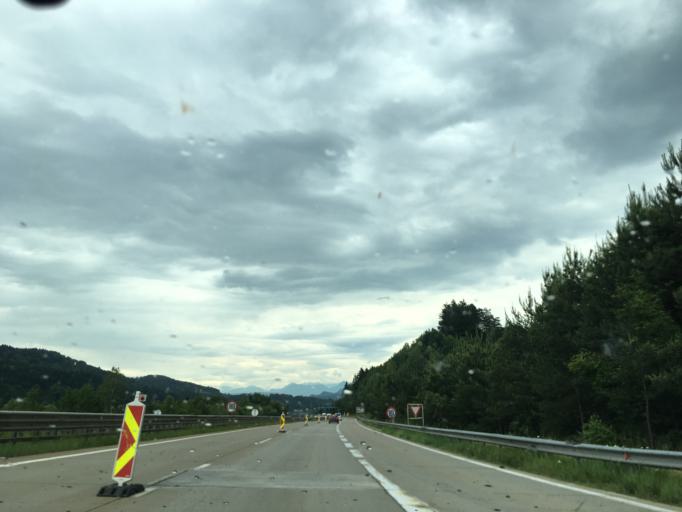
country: AT
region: Carinthia
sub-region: Villach Stadt
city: Villach
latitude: 46.6433
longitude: 13.7961
